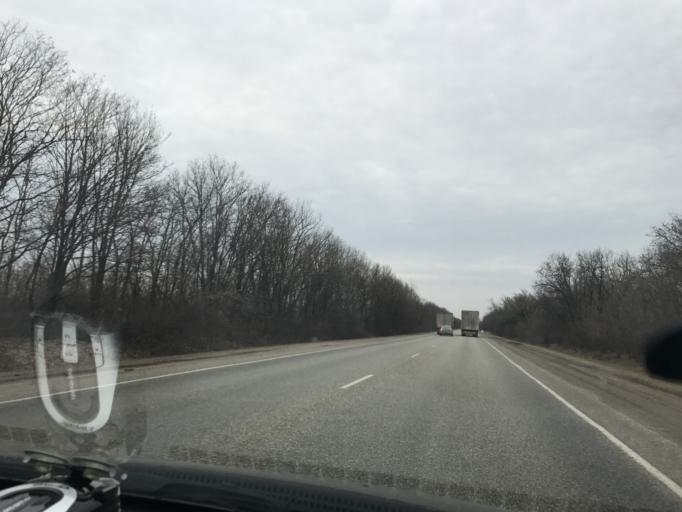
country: RU
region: Krasnodarskiy
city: Mirskoy
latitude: 45.5137
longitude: 40.4771
